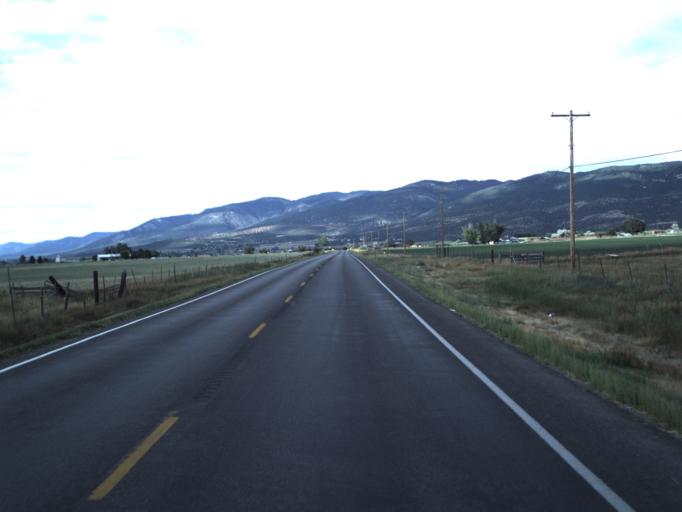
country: US
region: Utah
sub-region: Sanpete County
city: Fairview
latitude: 39.5888
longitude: -111.4503
